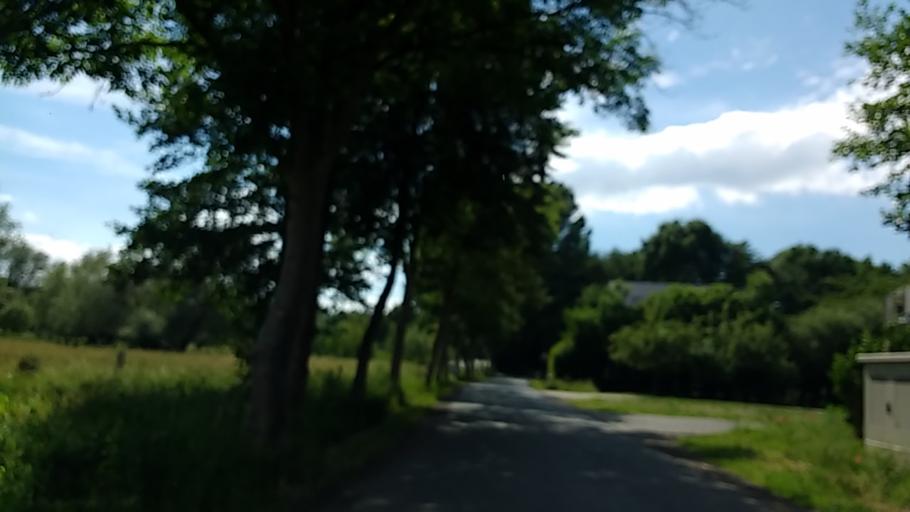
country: DE
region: North Rhine-Westphalia
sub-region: Regierungsbezirk Detmold
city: Salzkotten
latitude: 51.7251
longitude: 8.6644
